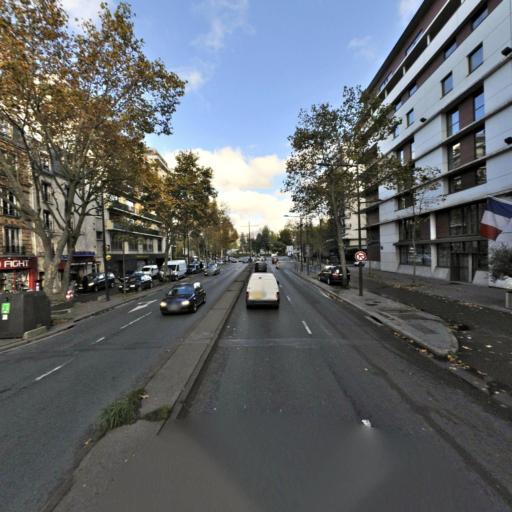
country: FR
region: Ile-de-France
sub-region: Departement des Hauts-de-Seine
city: Boulogne-Billancourt
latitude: 48.8364
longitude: 2.2525
